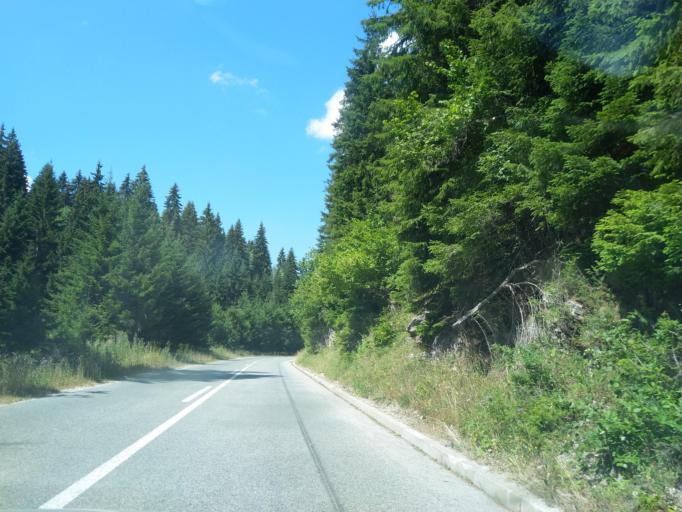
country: RS
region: Central Serbia
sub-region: Zlatiborski Okrug
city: Nova Varos
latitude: 43.3963
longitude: 19.8441
